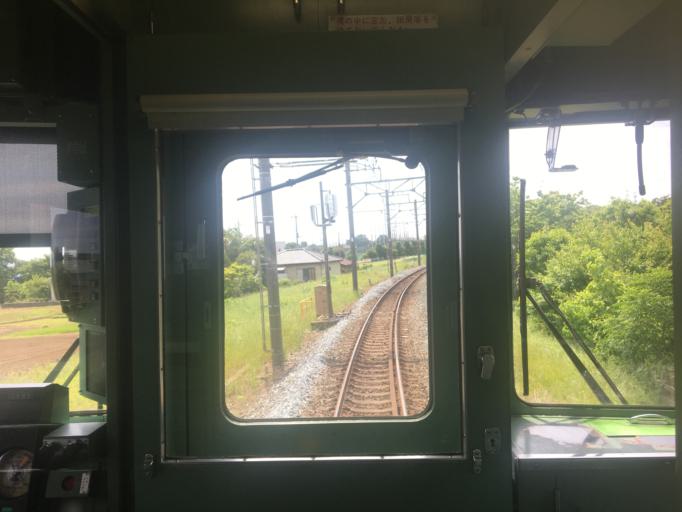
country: JP
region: Saitama
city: Morohongo
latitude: 35.9364
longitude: 139.3489
